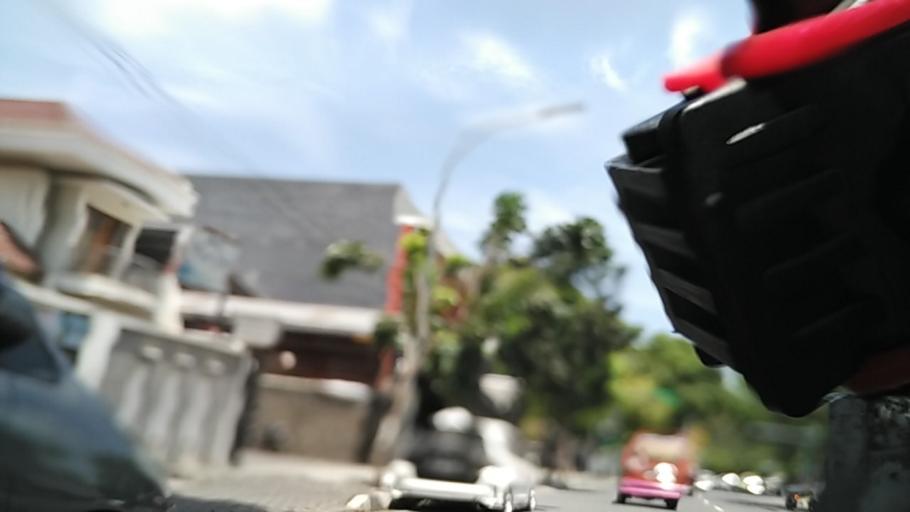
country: ID
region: Central Java
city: Semarang
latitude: -6.9880
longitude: 110.3826
